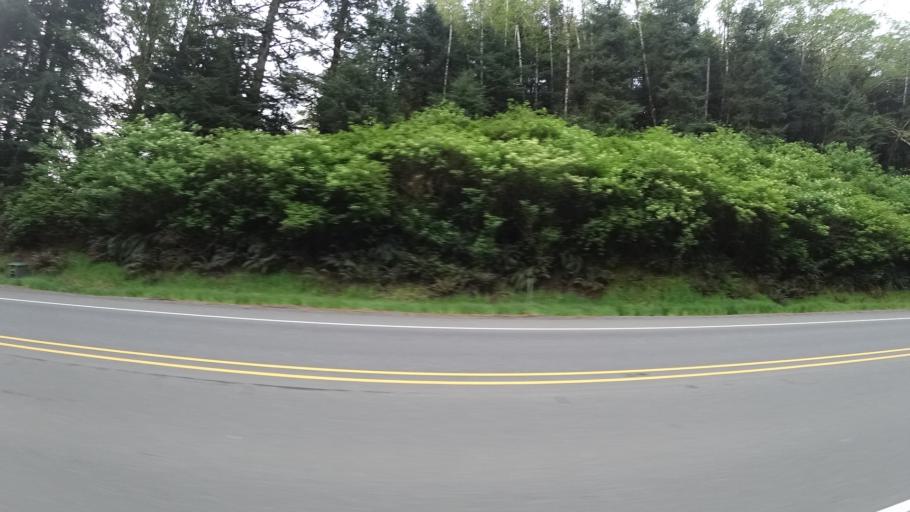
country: US
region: Oregon
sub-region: Coos County
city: Barview
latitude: 43.2547
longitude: -124.2753
